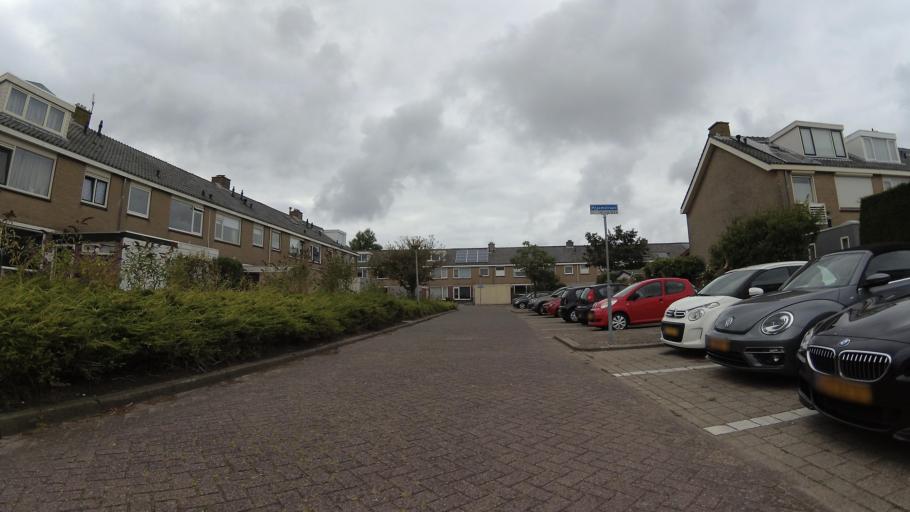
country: NL
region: North Holland
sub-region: Gemeente Den Helder
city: Den Helder
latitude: 52.9337
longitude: 4.7425
